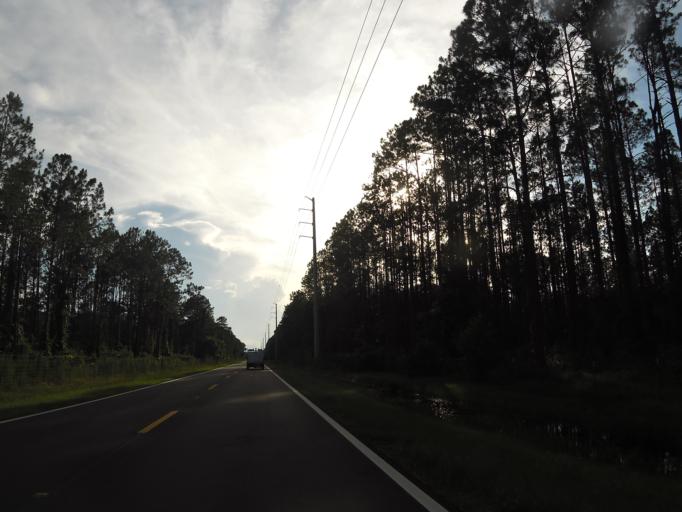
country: US
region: Florida
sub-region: Clay County
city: Green Cove Springs
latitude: 30.0146
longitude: -81.5893
